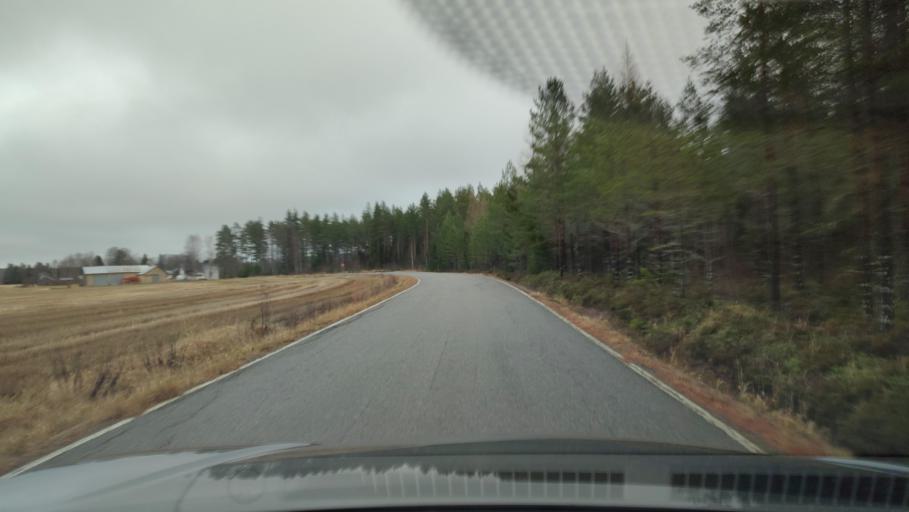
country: FI
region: Southern Ostrobothnia
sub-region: Suupohja
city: Isojoki
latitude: 62.1752
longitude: 21.9034
